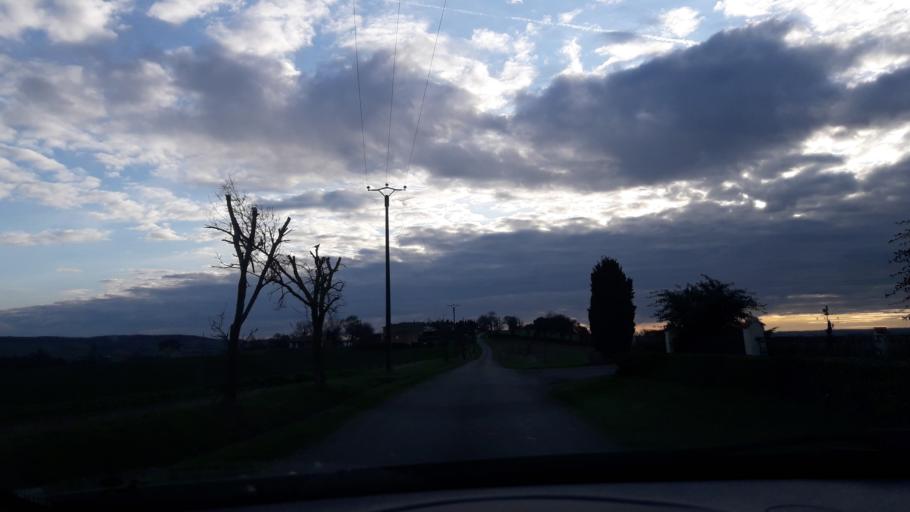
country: FR
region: Midi-Pyrenees
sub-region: Departement du Gers
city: Pujaudran
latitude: 43.6665
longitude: 1.0555
